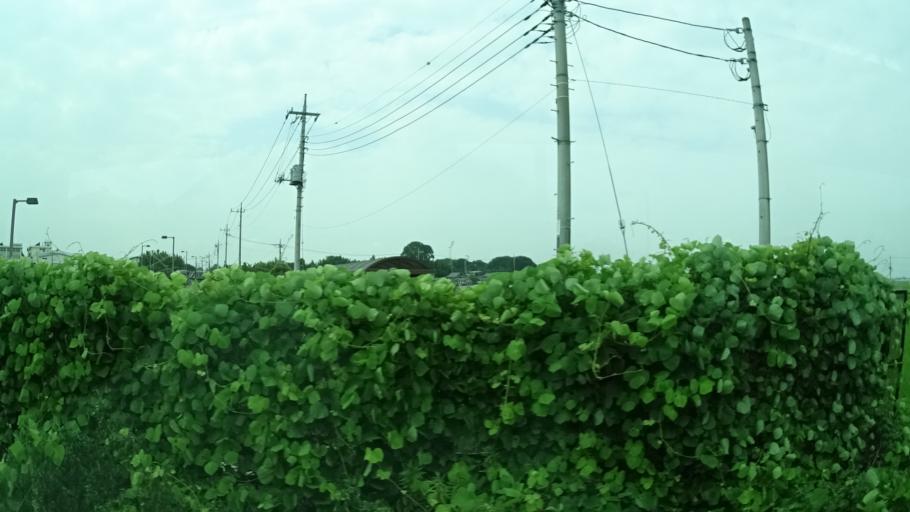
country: JP
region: Tochigi
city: Mooka
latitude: 36.4475
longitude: 140.0078
